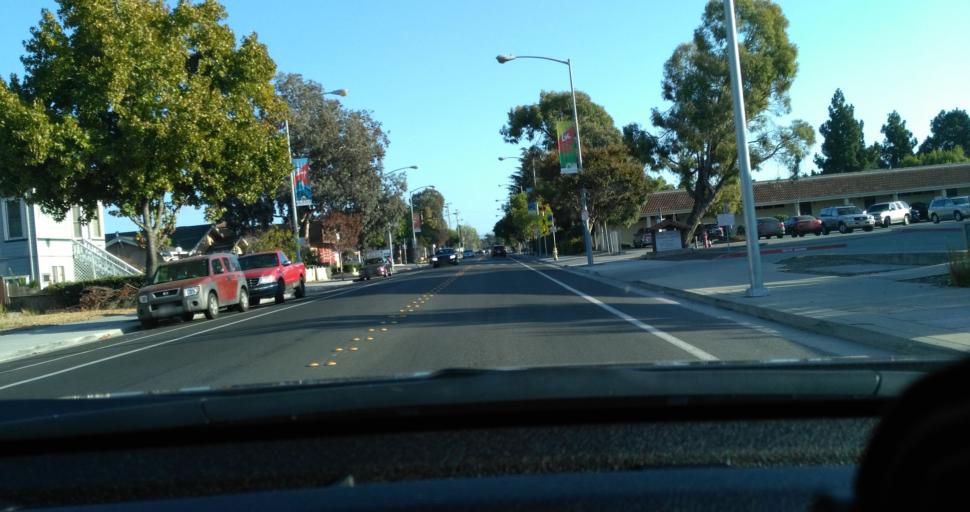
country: US
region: California
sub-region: Santa Clara County
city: Milpitas
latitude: 37.4269
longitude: -121.9060
